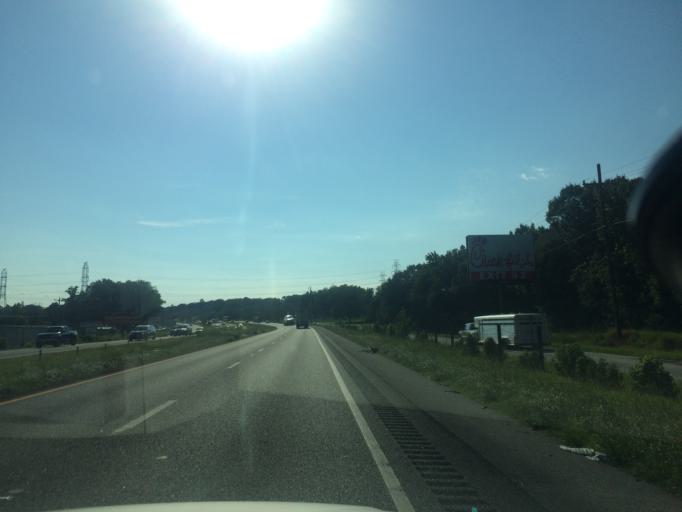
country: US
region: South Carolina
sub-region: Cherokee County
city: East Gaffney
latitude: 35.1025
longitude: -81.6386
